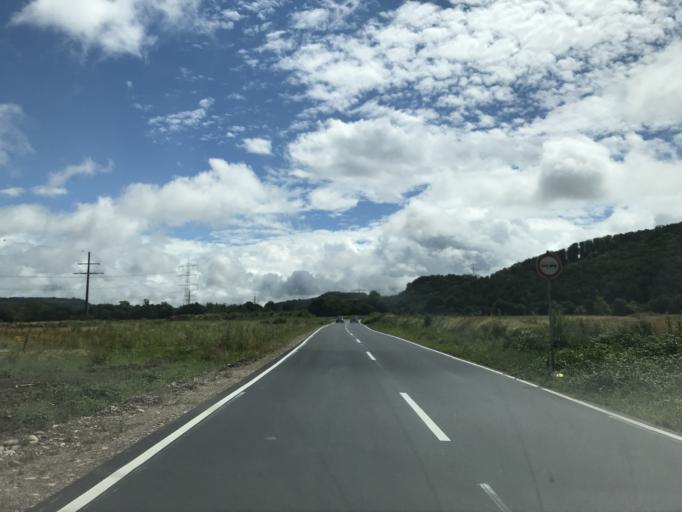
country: DE
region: Baden-Wuerttemberg
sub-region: Freiburg Region
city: Steinen
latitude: 47.6410
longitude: 7.7086
